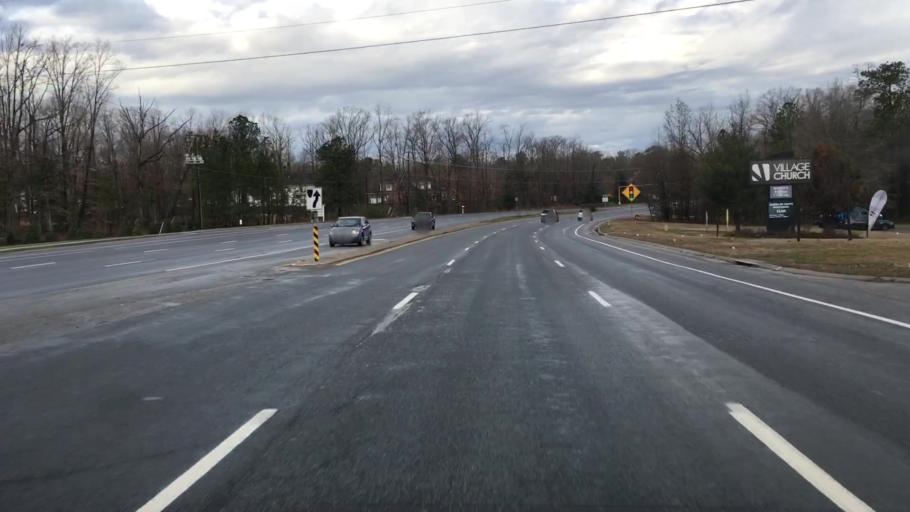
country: US
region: Virginia
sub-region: Chesterfield County
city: Bon Air
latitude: 37.4946
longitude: -77.6035
